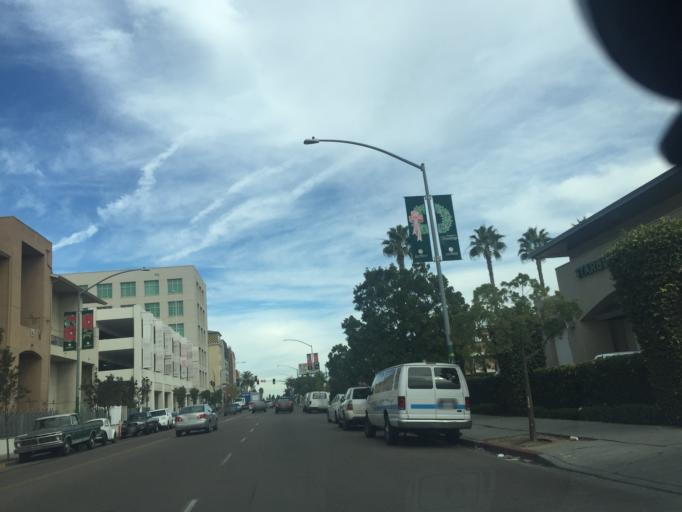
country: US
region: California
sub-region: San Diego County
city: San Diego
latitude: 32.7483
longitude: -117.1009
